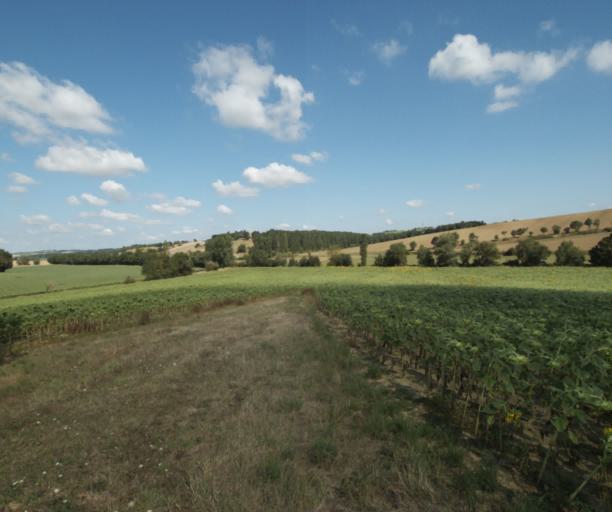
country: FR
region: Midi-Pyrenees
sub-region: Departement de la Haute-Garonne
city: Avignonet-Lauragais
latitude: 43.4457
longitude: 1.7851
